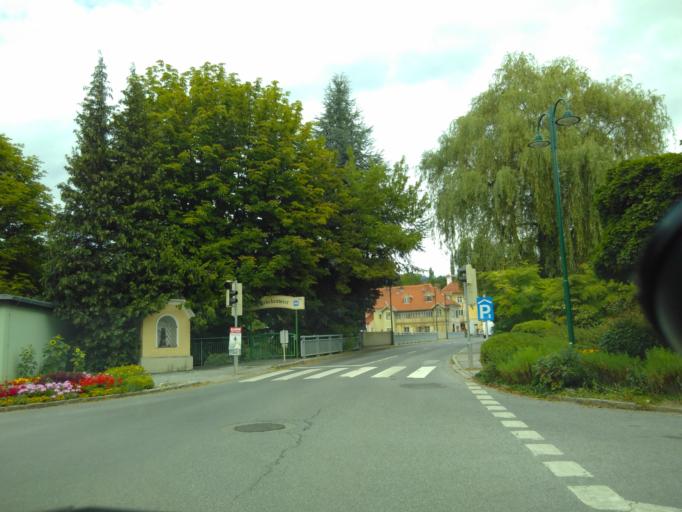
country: AT
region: Styria
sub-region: Politischer Bezirk Graz-Umgebung
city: Frohnleiten
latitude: 47.2683
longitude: 15.3253
